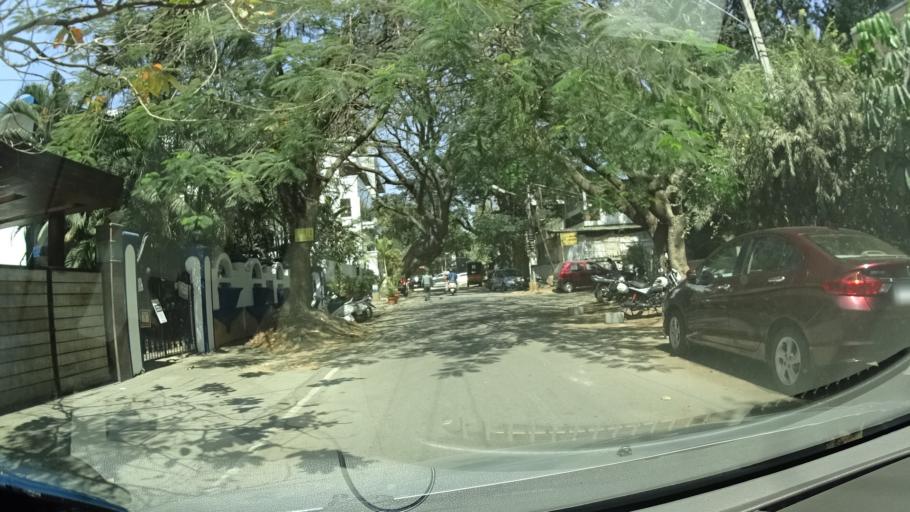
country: IN
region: Karnataka
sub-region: Bangalore Urban
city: Bangalore
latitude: 12.9694
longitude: 77.6420
